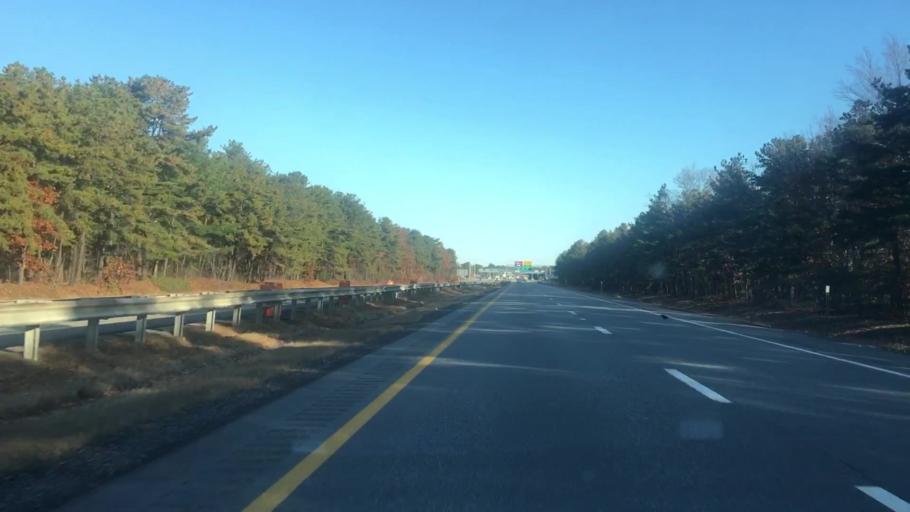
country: US
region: Maine
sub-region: Cumberland County
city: New Gloucester
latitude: 43.9292
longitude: -70.3361
